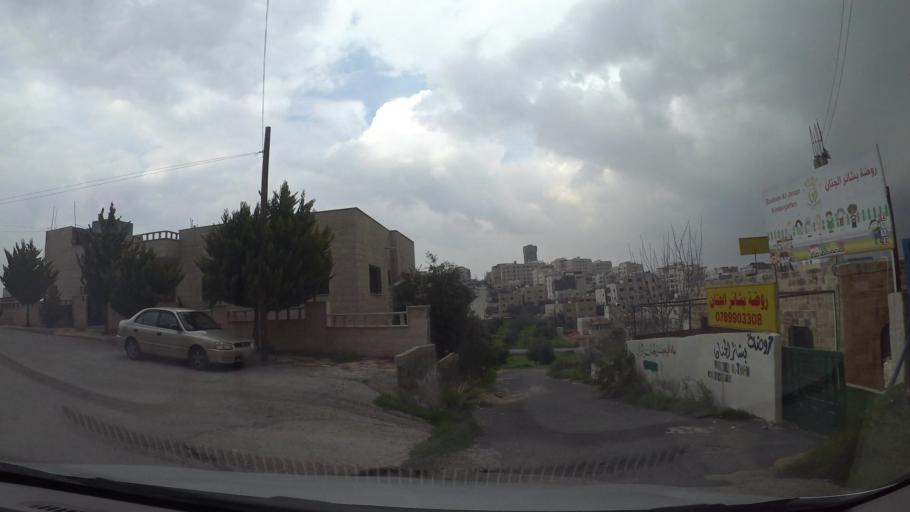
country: JO
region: Amman
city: Umm as Summaq
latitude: 31.8832
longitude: 35.8590
